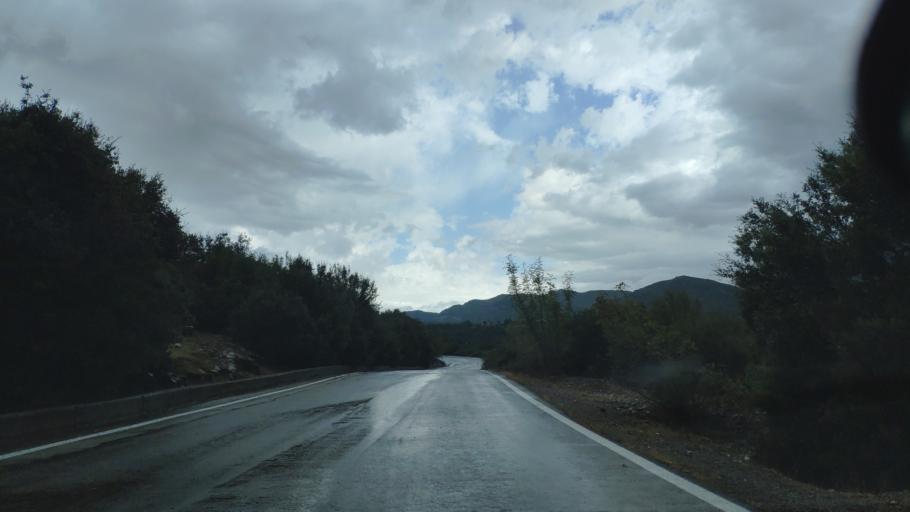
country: GR
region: Central Greece
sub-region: Nomos Evrytanias
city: Kerasochori
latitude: 39.1027
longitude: 21.4331
